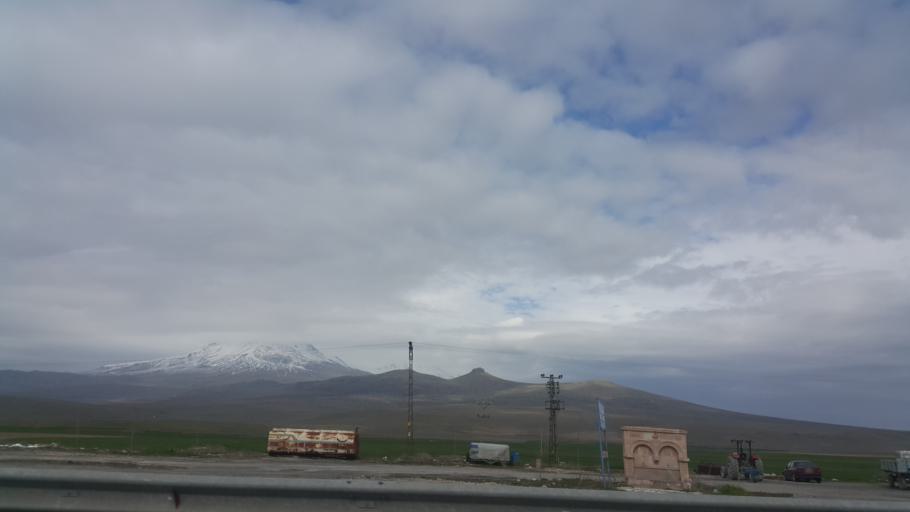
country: TR
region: Aksaray
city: Taspinar
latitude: 38.0411
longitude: 34.0368
